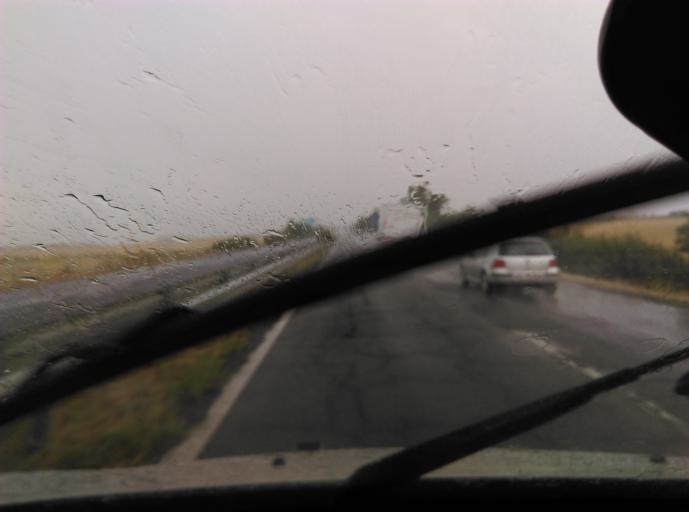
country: BG
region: Burgas
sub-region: Obshtina Burgas
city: Burgas
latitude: 42.5834
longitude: 27.4032
